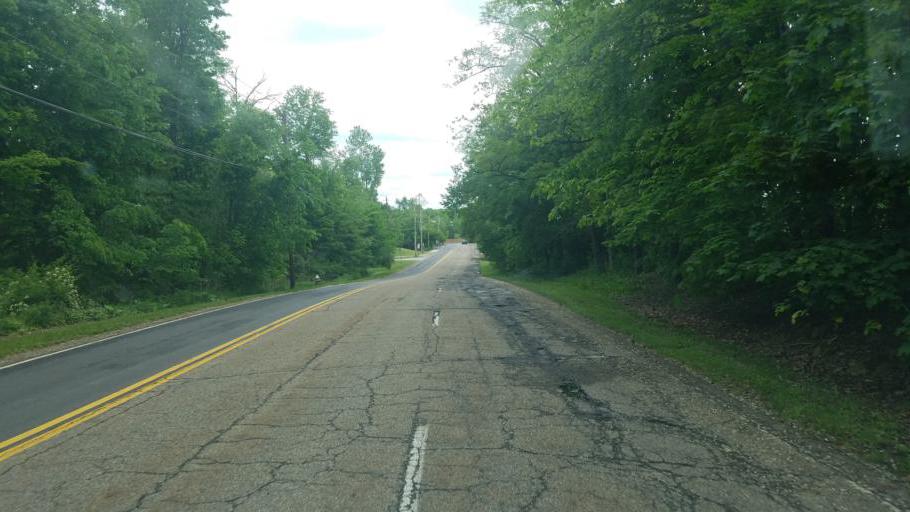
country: US
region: Ohio
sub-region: Summit County
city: Reminderville
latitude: 41.3454
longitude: -81.3684
